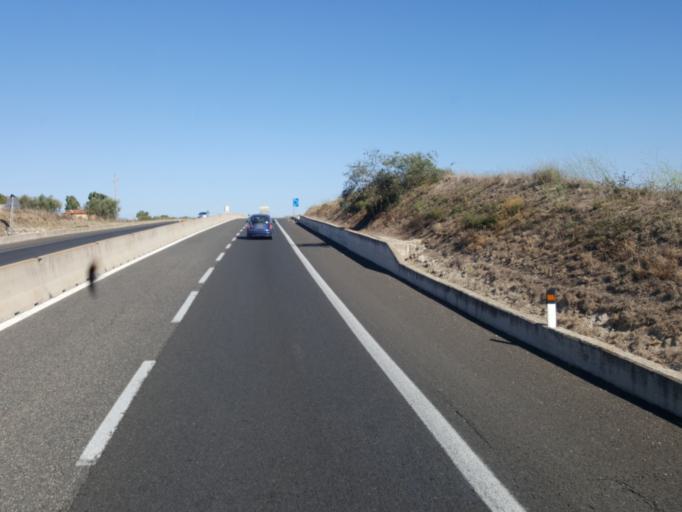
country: IT
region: Latium
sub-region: Provincia di Viterbo
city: Montalto di Castro
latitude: 42.3598
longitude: 11.5856
